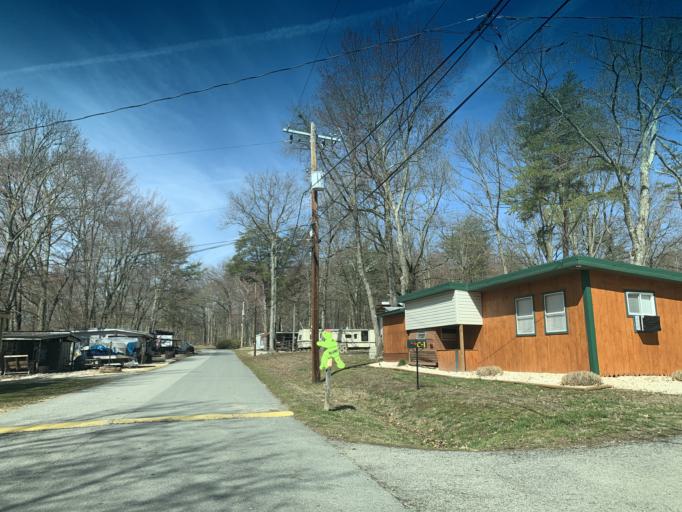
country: US
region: Maryland
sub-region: Cecil County
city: Charlestown
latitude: 39.5523
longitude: -76.0083
